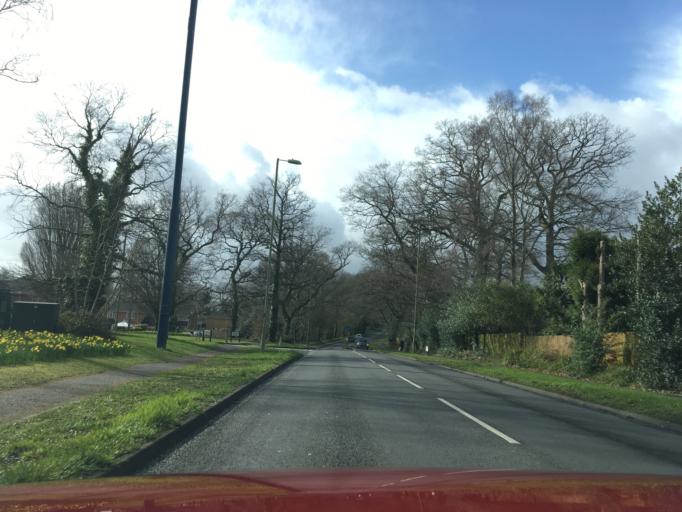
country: GB
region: England
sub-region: Hampshire
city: Chandlers Ford
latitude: 50.9922
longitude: -1.3674
